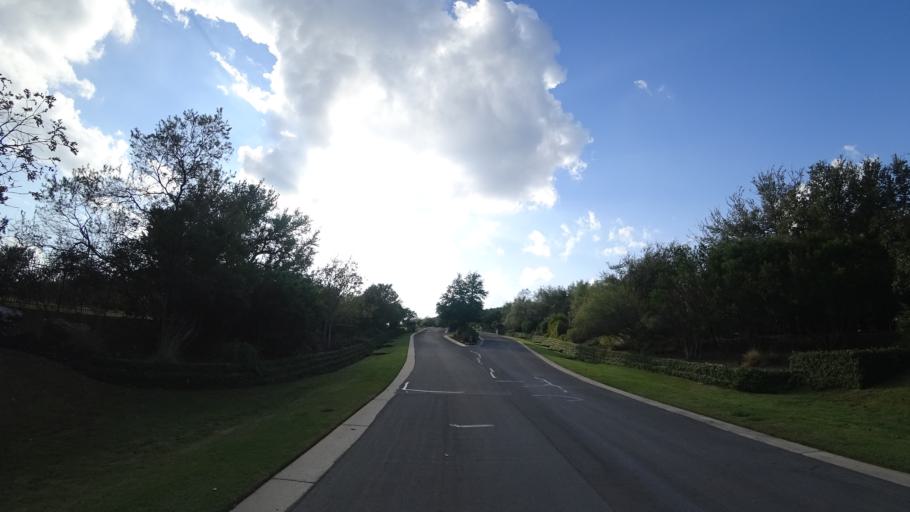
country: US
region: Texas
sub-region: Travis County
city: Barton Creek
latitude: 30.2741
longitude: -97.8635
